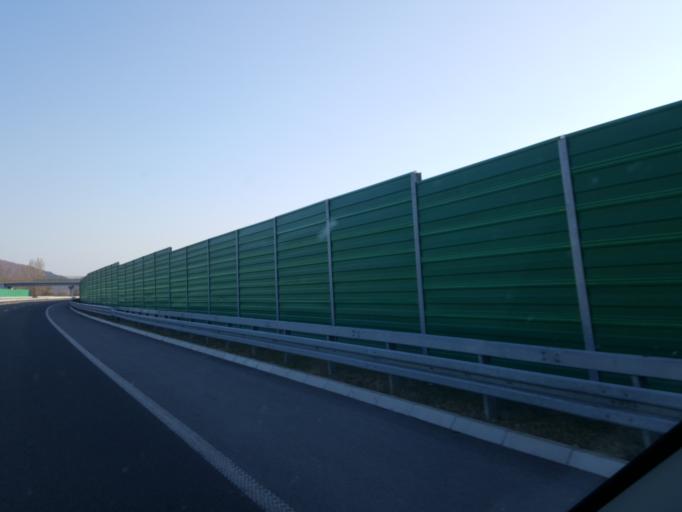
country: RS
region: Central Serbia
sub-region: Pirotski Okrug
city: Dimitrovgrad
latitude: 43.0475
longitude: 22.7042
